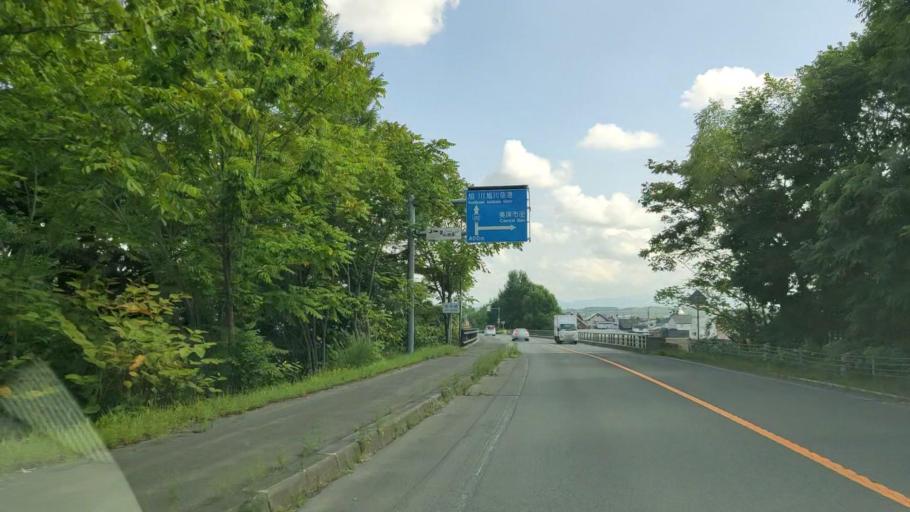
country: JP
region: Hokkaido
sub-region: Asahikawa-shi
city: Asahikawa
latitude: 43.5884
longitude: 142.4500
